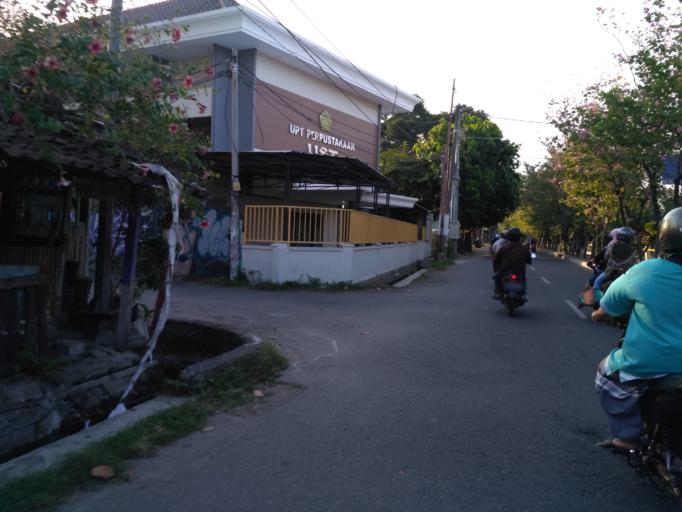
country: ID
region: Daerah Istimewa Yogyakarta
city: Yogyakarta
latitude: -7.8064
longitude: 110.3814
